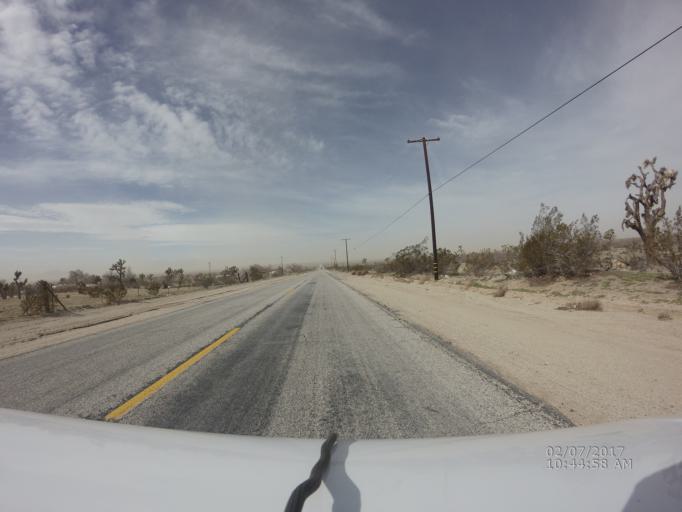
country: US
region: California
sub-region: Los Angeles County
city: Lake Los Angeles
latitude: 34.6899
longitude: -117.8343
